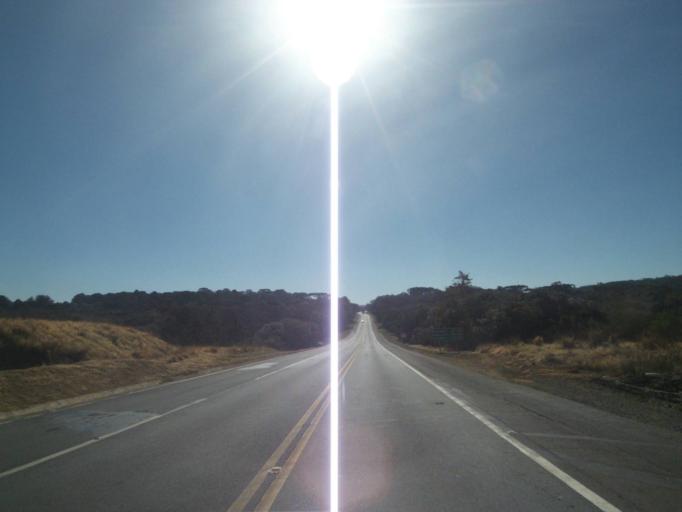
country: BR
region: Parana
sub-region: Tibagi
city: Tibagi
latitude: -24.7411
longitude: -50.5376
